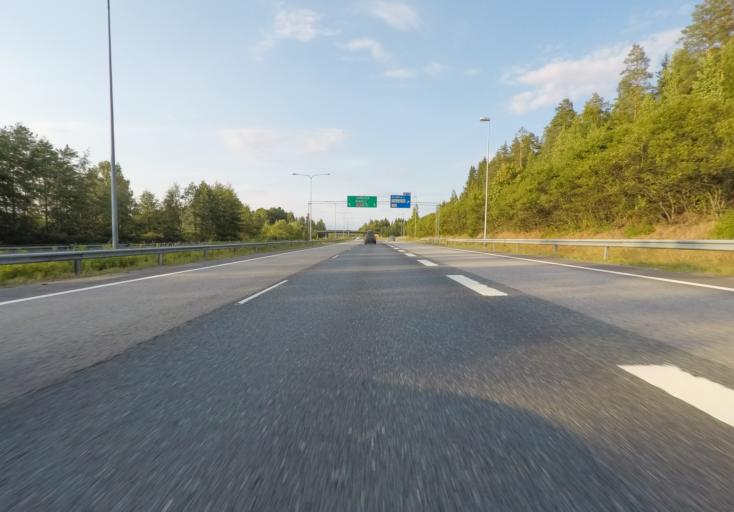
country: FI
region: Paijanne Tavastia
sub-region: Lahti
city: Heinola
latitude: 61.1874
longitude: 26.0000
